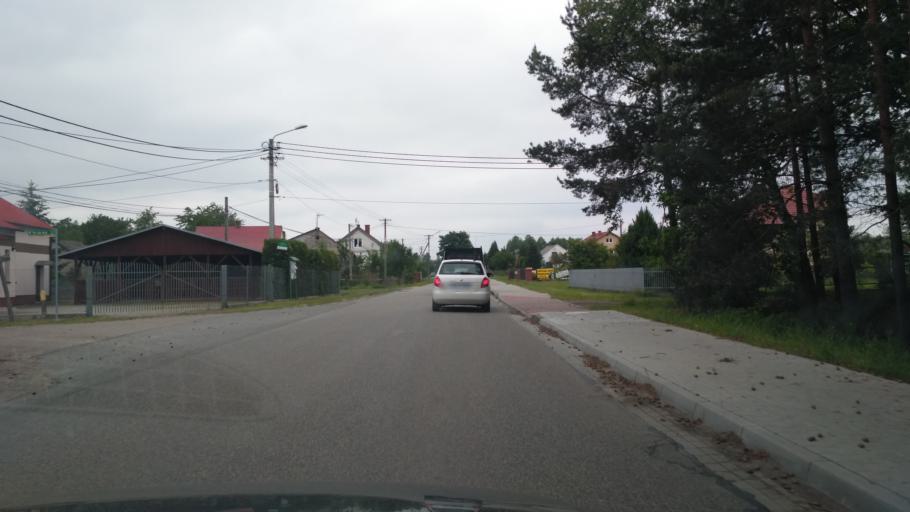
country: PL
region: Subcarpathian Voivodeship
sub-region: Powiat ropczycko-sedziszowski
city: Sedziszow Malopolski
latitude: 50.1456
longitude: 21.6701
